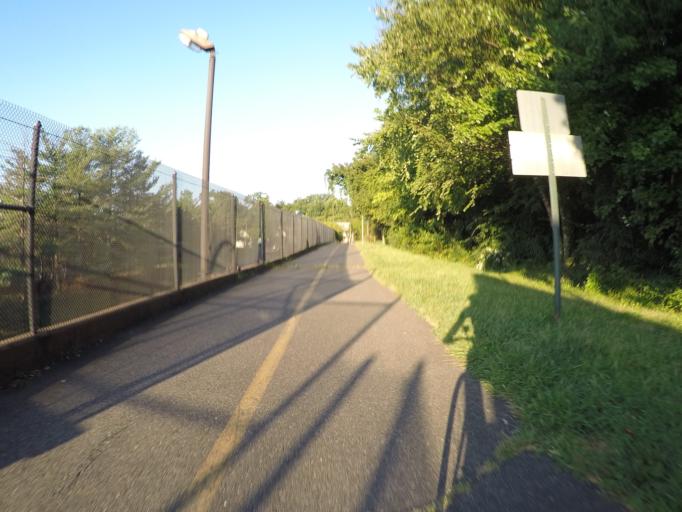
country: US
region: Virginia
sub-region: Arlington County
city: Arlington
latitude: 38.8878
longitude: -77.1168
